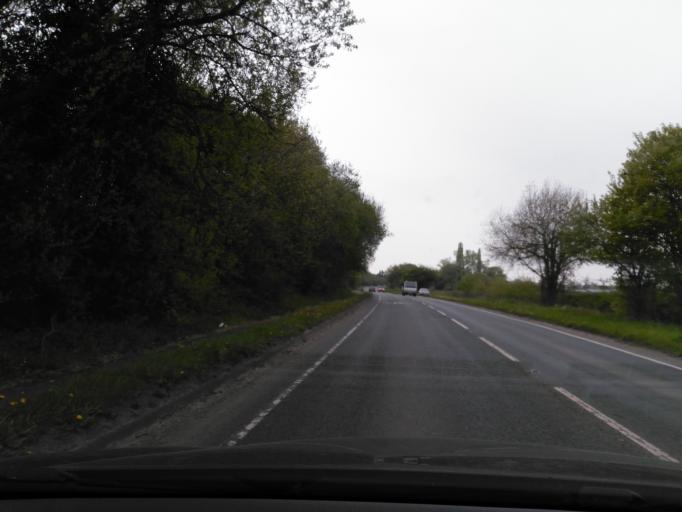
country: GB
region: England
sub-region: Hampshire
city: Tadley
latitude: 51.3372
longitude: -1.1279
